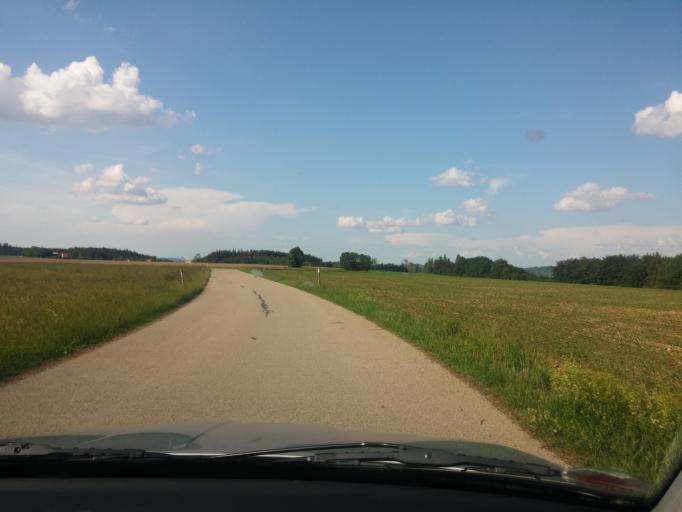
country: DE
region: Bavaria
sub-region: Swabia
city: Woringen
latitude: 47.8858
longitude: 10.1969
